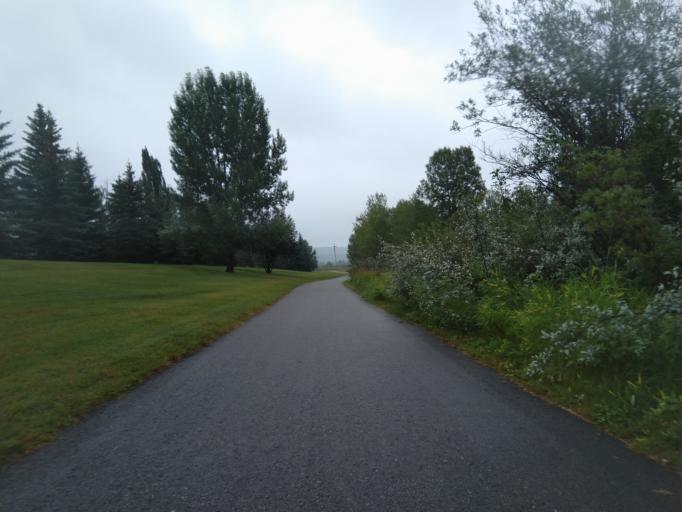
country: CA
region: Alberta
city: Cochrane
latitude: 51.1731
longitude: -114.4713
